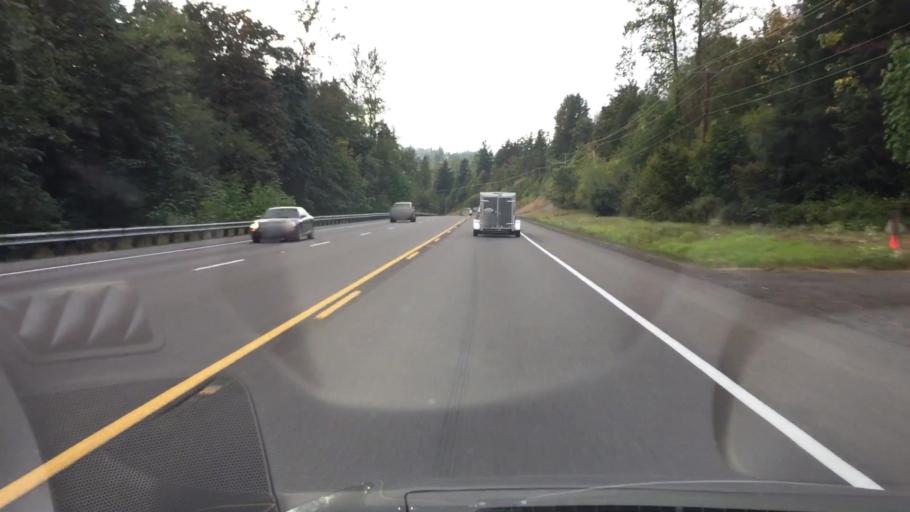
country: US
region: Washington
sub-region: Lewis County
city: Napavine
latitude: 46.5308
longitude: -122.6083
